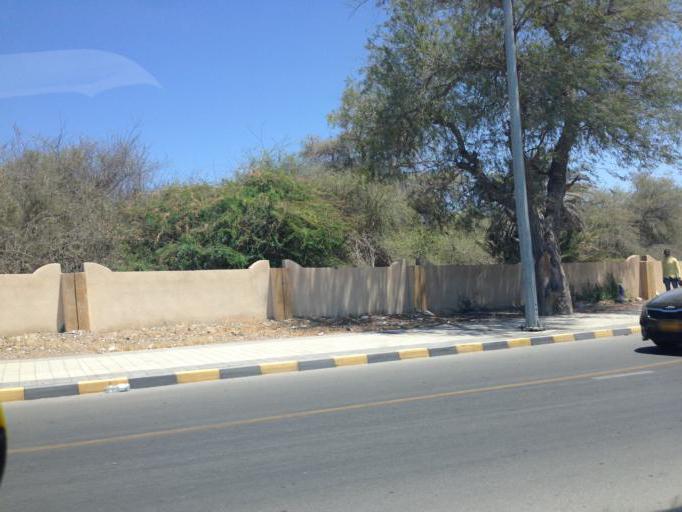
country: OM
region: Muhafazat Masqat
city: As Sib al Jadidah
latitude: 23.6623
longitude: 58.2040
